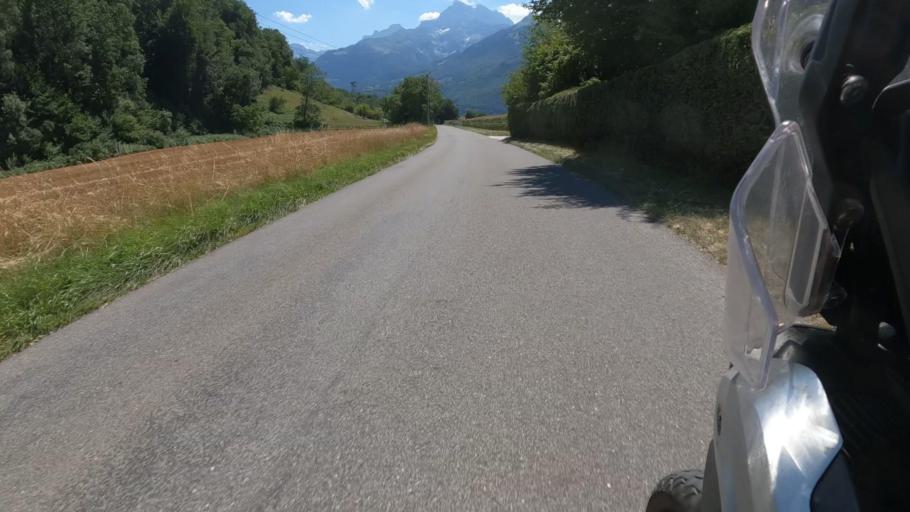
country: CH
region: Vaud
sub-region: Aigle District
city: Bex
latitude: 46.2664
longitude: 7.0055
